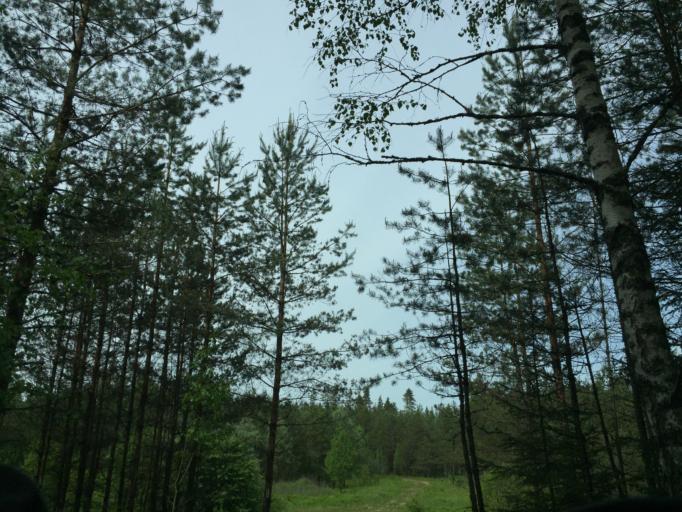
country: LV
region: Koceni
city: Koceni
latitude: 57.4748
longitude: 25.3796
